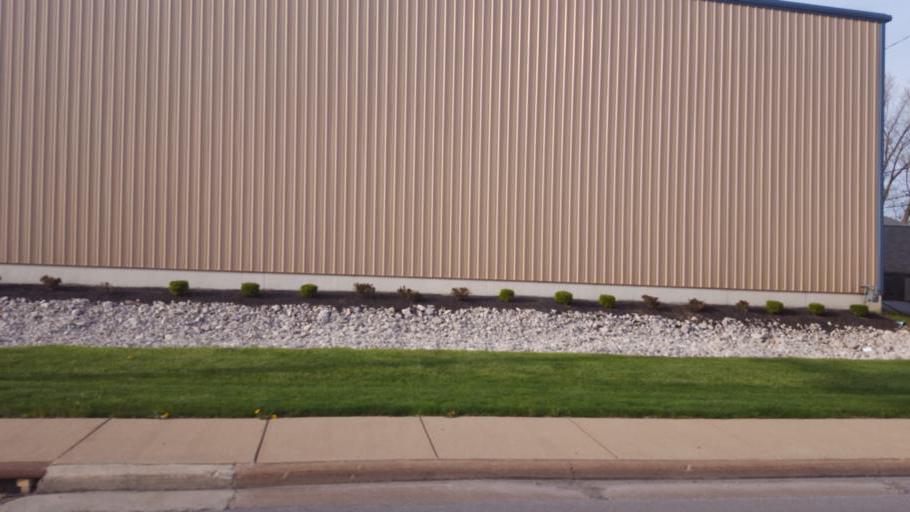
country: US
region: Ohio
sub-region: Erie County
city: Sandusky
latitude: 41.4504
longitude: -82.6761
